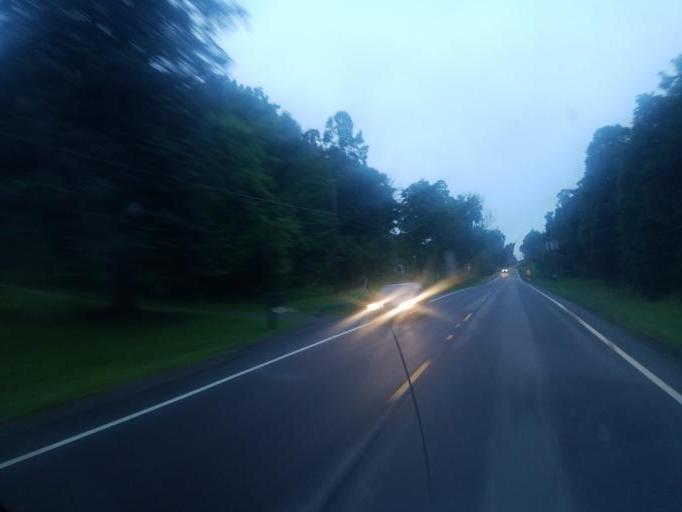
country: US
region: Ohio
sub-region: Carroll County
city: Carrollton
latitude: 40.5430
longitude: -81.0337
